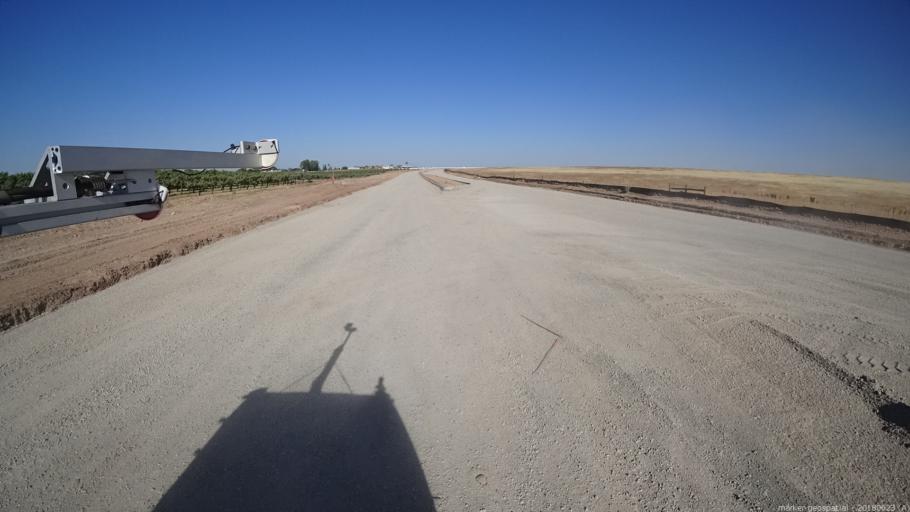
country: US
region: California
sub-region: Madera County
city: Bonadelle Ranchos-Madera Ranchos
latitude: 36.9668
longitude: -119.7885
